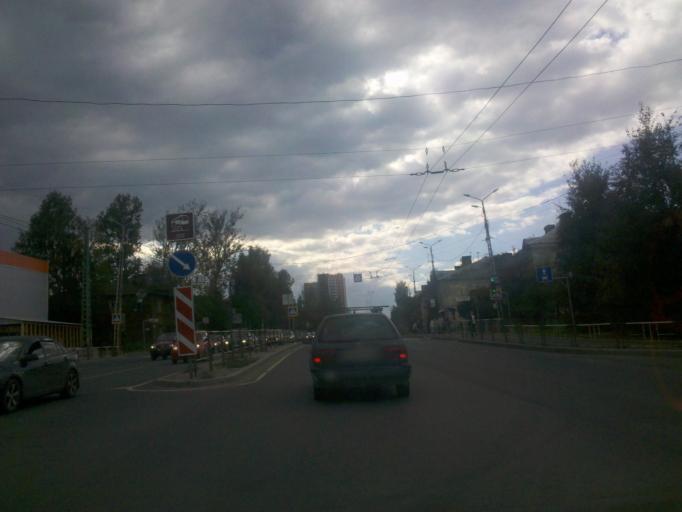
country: RU
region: Republic of Karelia
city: Petrozavodsk
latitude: 61.7883
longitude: 34.3391
